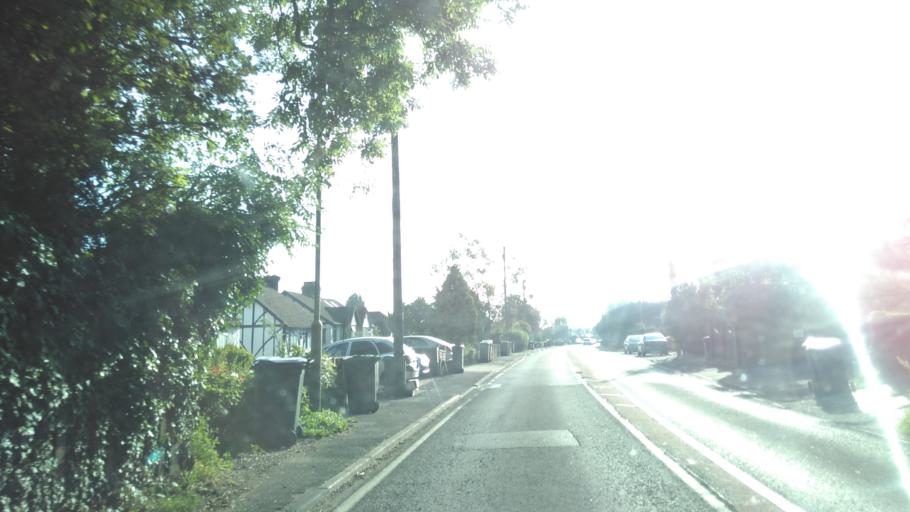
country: GB
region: England
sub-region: Kent
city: Chartham
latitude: 51.2684
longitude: 1.0448
